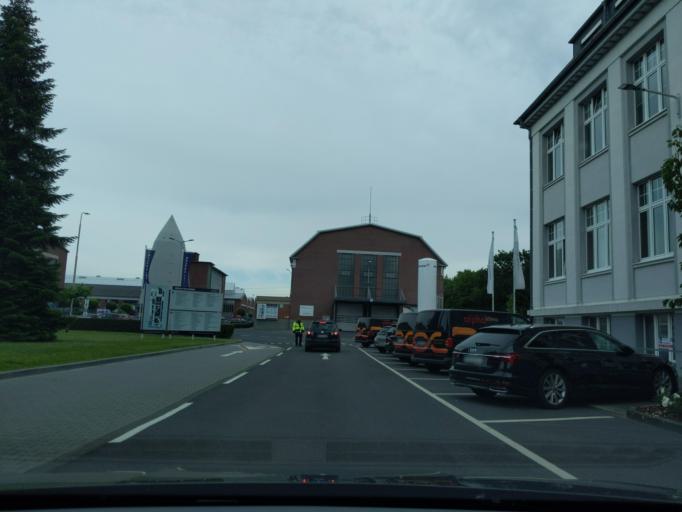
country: DE
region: North Rhine-Westphalia
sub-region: Regierungsbezirk Dusseldorf
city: Meerbusch
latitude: 51.2450
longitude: 6.7159
